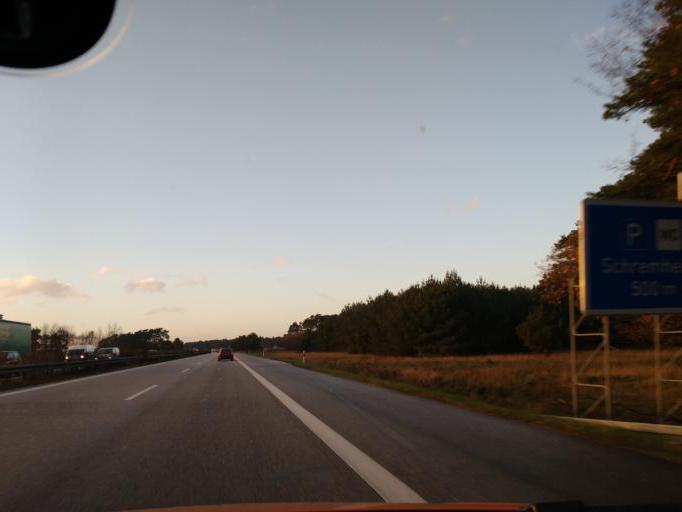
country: DE
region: Mecklenburg-Vorpommern
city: Sulstorf
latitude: 53.4574
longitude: 11.3528
